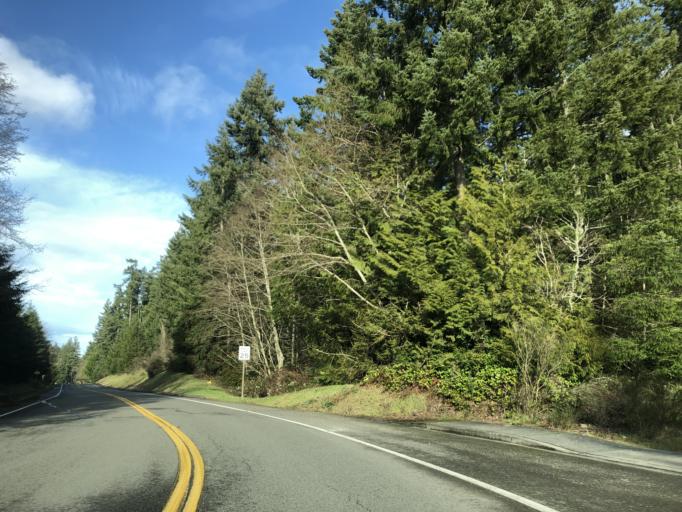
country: US
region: Washington
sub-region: Kitsap County
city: Poulsbo
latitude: 47.7658
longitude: -122.6546
